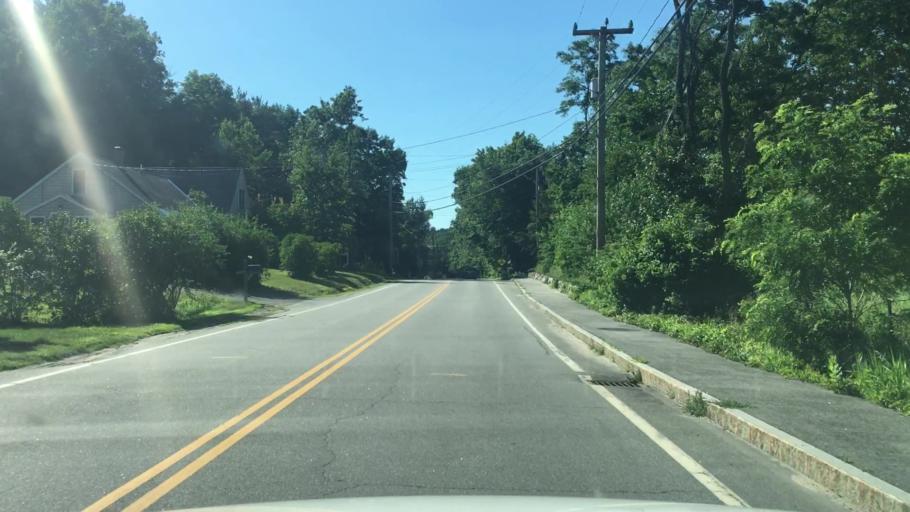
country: US
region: New Hampshire
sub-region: Rockingham County
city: Newmarket
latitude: 43.0361
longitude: -70.9457
